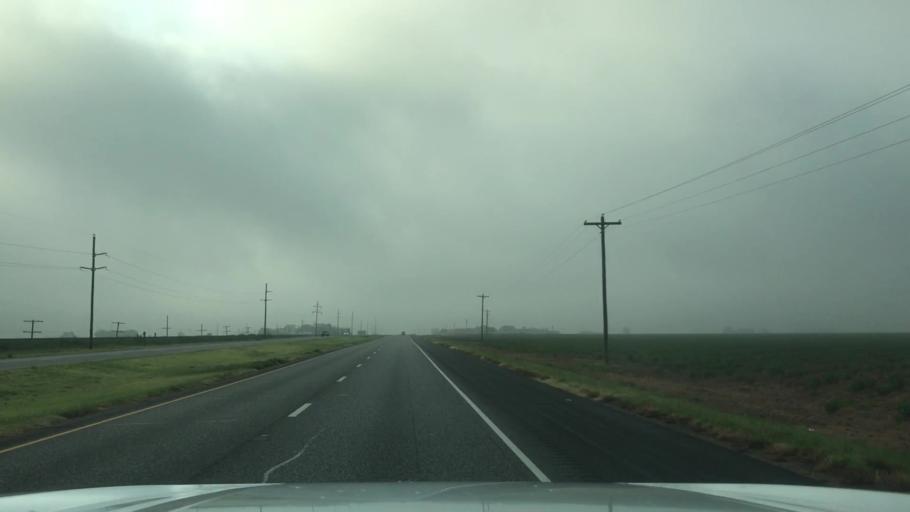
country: US
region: Texas
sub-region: Lubbock County
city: Ransom Canyon
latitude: 33.4879
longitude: -101.7203
